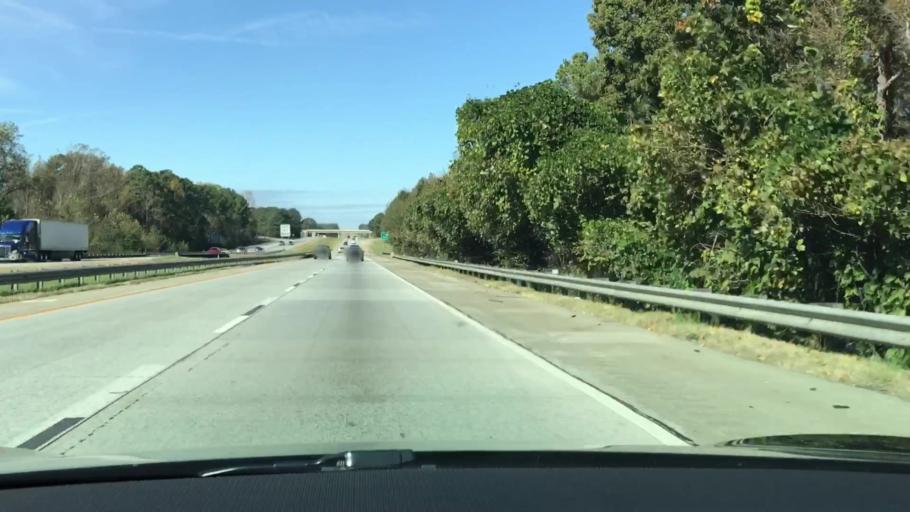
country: US
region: Georgia
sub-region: Morgan County
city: Madison
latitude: 33.5575
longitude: -83.4906
